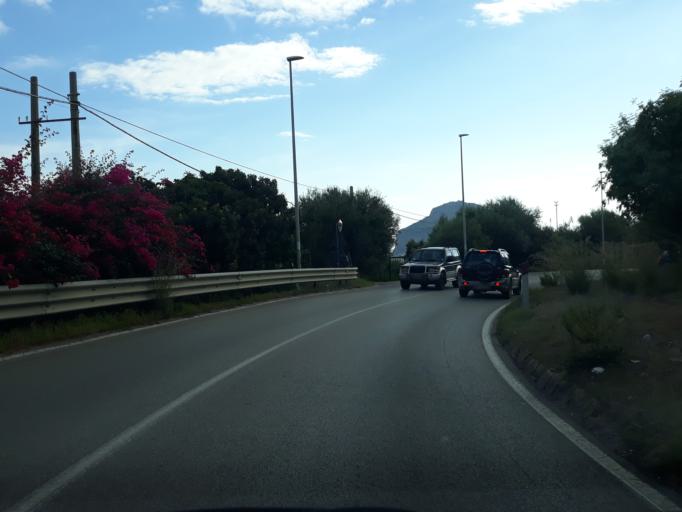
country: IT
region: Sicily
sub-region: Palermo
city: Cefalu
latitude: 38.0292
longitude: 13.9915
